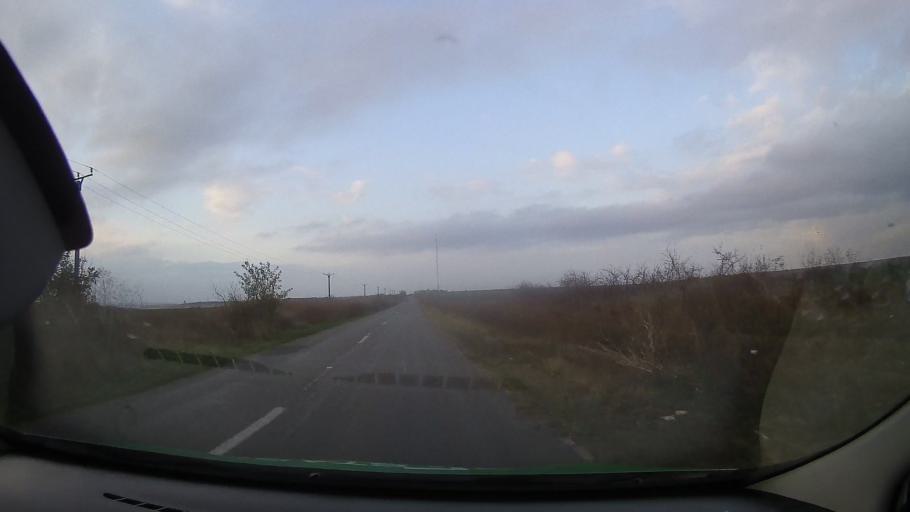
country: RO
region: Constanta
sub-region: Comuna Dobromir
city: Dobromir
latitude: 44.0384
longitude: 27.7581
